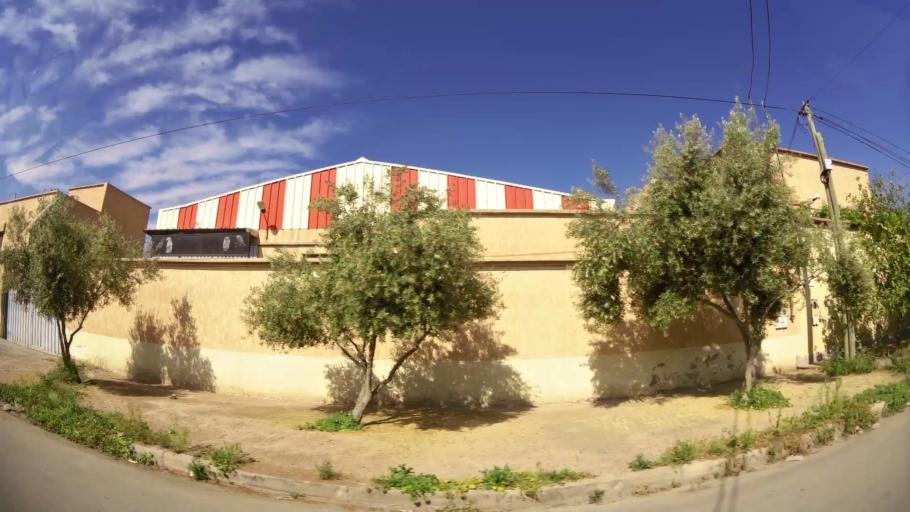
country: MA
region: Oriental
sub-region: Oujda-Angad
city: Oujda
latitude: 34.7042
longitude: -1.8865
